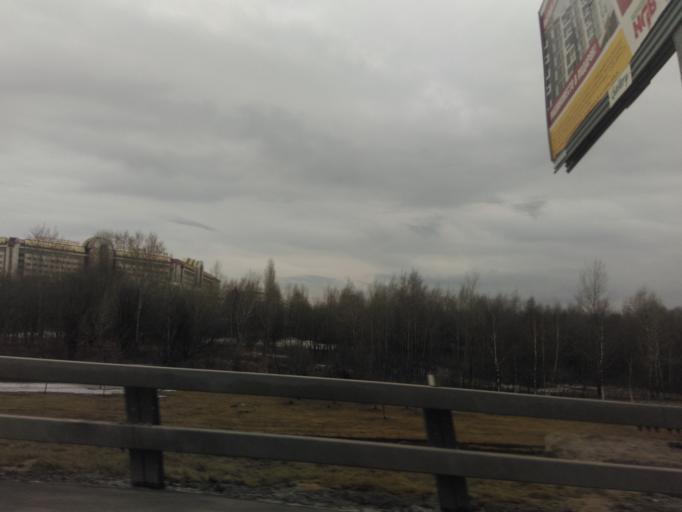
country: RU
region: Moscow
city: Rublevo
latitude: 55.7657
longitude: 37.3770
